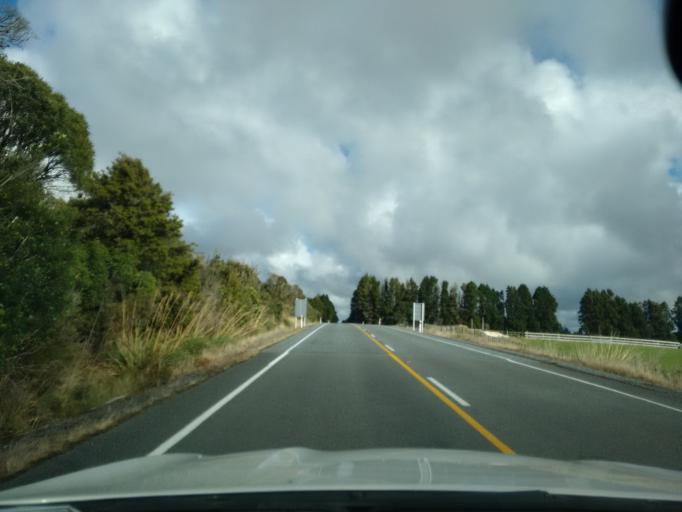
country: NZ
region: Manawatu-Wanganui
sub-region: Ruapehu District
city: Waiouru
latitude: -39.2817
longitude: 175.3864
